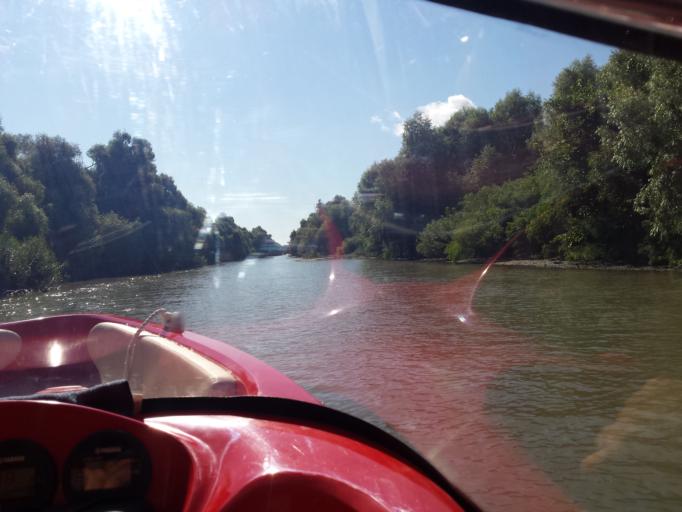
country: RO
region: Tulcea
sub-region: Comuna Pardina
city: Pardina
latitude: 45.2529
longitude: 28.9789
